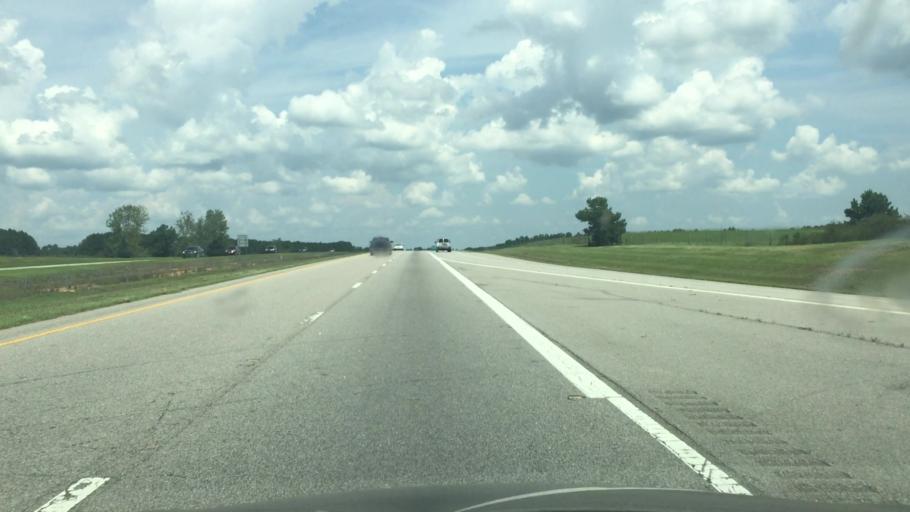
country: US
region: North Carolina
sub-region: Richmond County
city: Ellerbe
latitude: 35.1497
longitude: -79.7145
